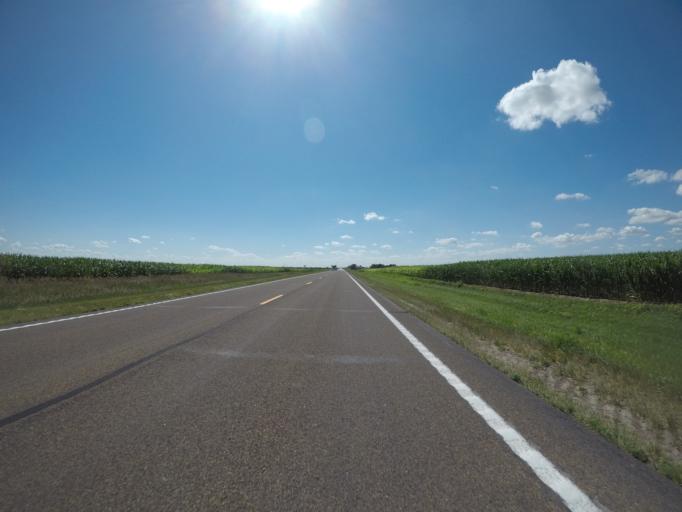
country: US
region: Nebraska
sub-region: Chase County
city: Imperial
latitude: 40.5378
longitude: -101.9249
